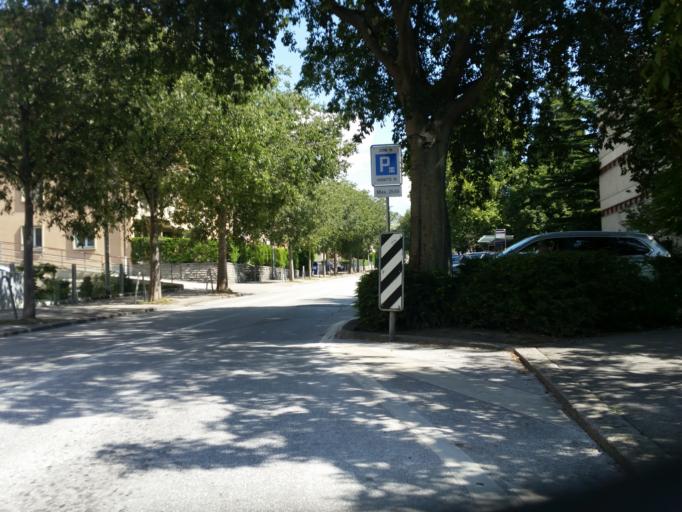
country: CH
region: Valais
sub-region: Sion District
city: Sitten
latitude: 46.2312
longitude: 7.3485
